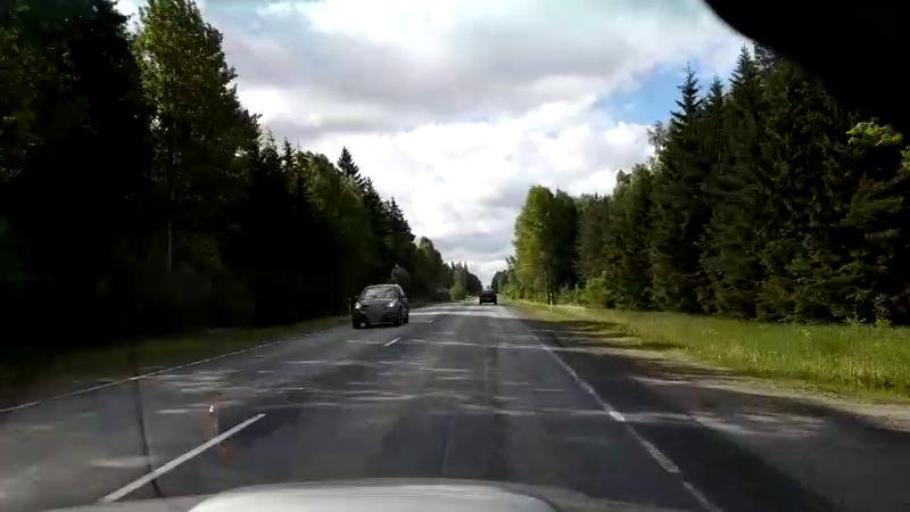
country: EE
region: Harju
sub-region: Saue linn
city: Saue
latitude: 59.2141
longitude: 24.4958
